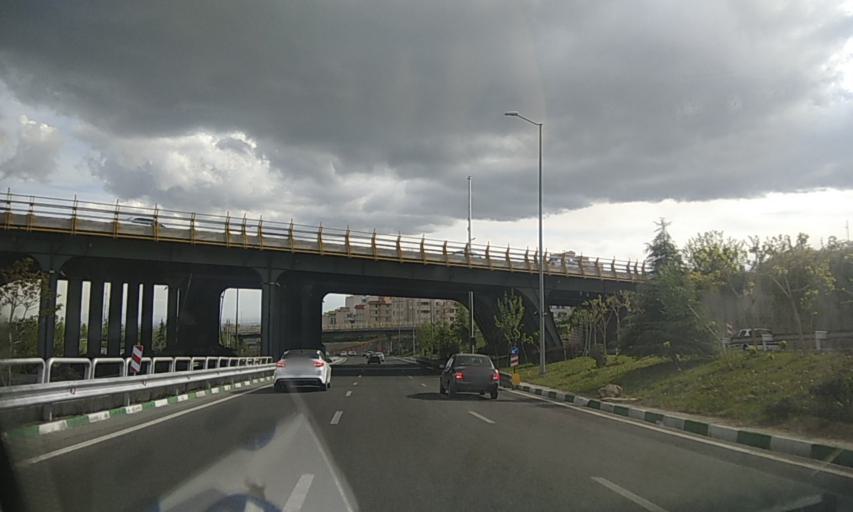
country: IR
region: Tehran
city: Tajrish
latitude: 35.7642
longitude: 51.2970
